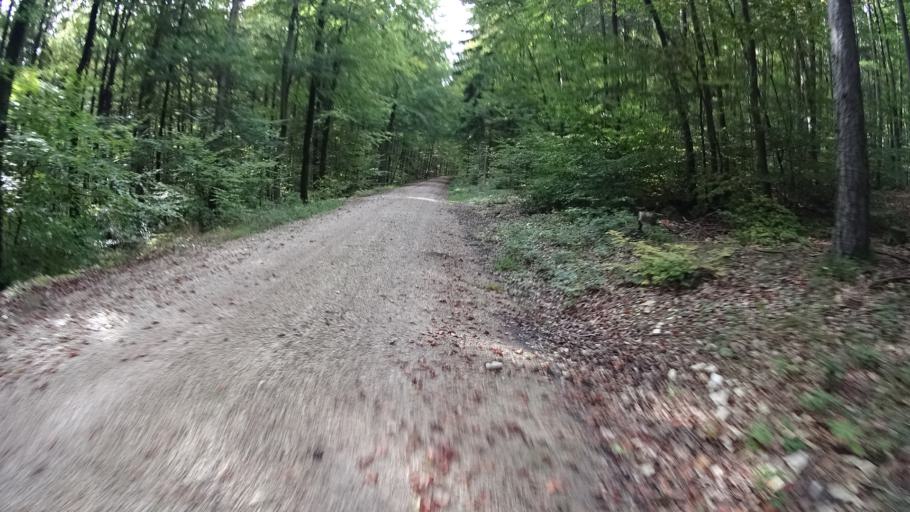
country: DE
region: Bavaria
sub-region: Upper Bavaria
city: Walting
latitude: 48.9056
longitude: 11.3167
